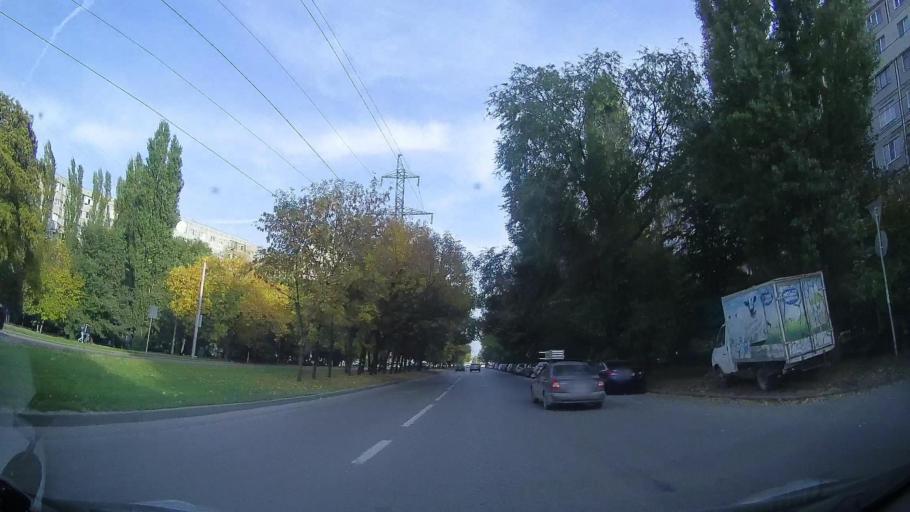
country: RU
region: Rostov
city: Imeni Chkalova
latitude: 47.2812
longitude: 39.7631
